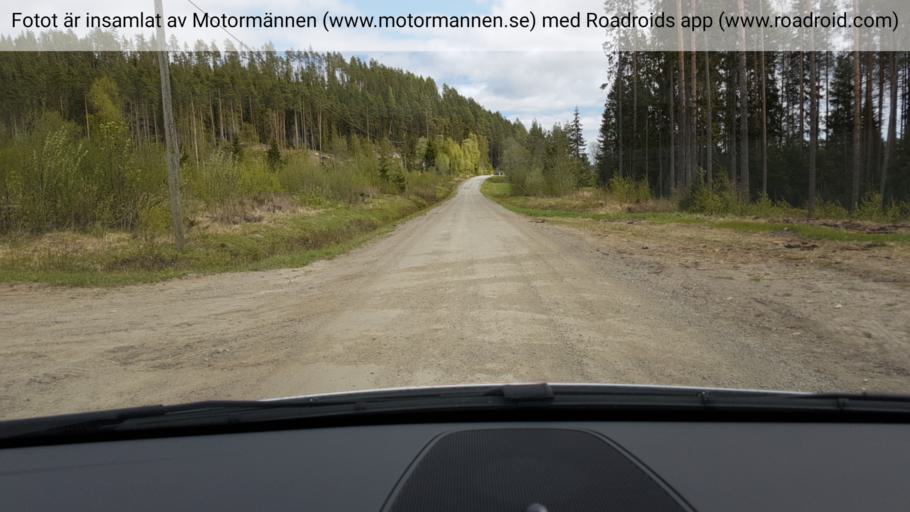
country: SE
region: Jaemtland
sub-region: OEstersunds Kommun
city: Brunflo
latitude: 62.8156
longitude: 15.0514
